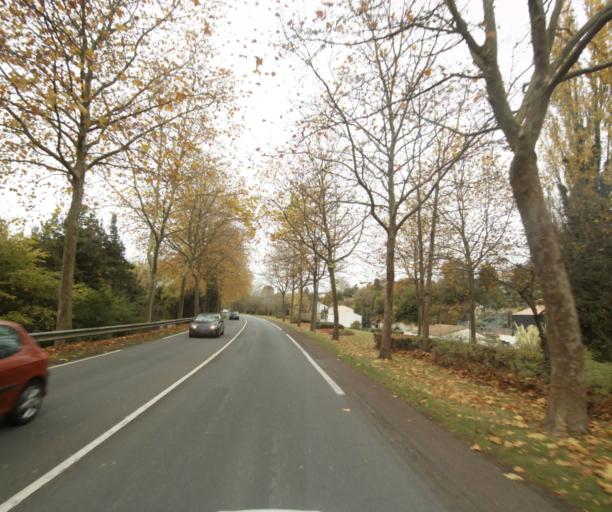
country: FR
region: Poitou-Charentes
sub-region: Departement de la Charente-Maritime
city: Saintes
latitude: 45.7420
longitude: -0.6442
